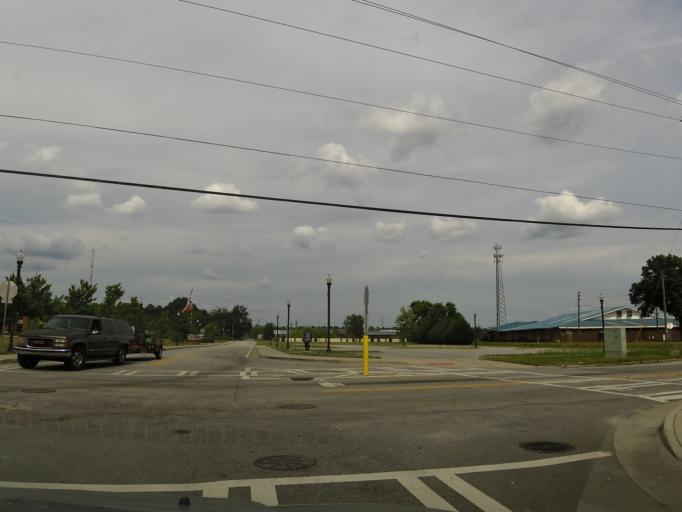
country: US
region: Georgia
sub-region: McDuffie County
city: Thomson
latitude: 33.4665
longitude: -82.5007
